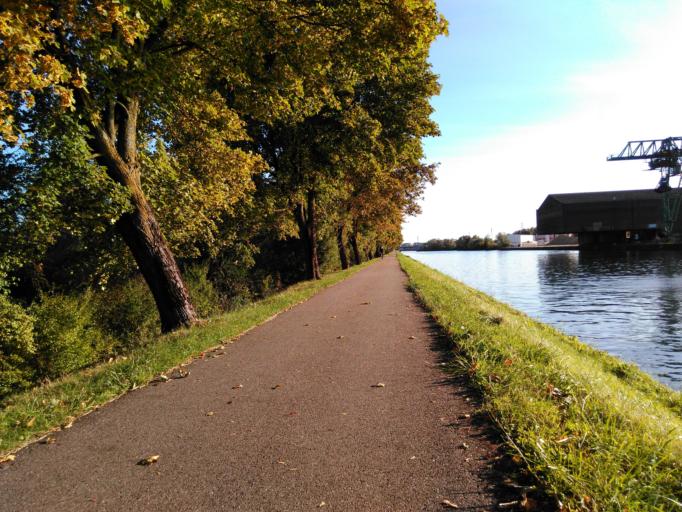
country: FR
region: Lorraine
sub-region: Departement de la Moselle
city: Mondelange
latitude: 49.2708
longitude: 6.1818
